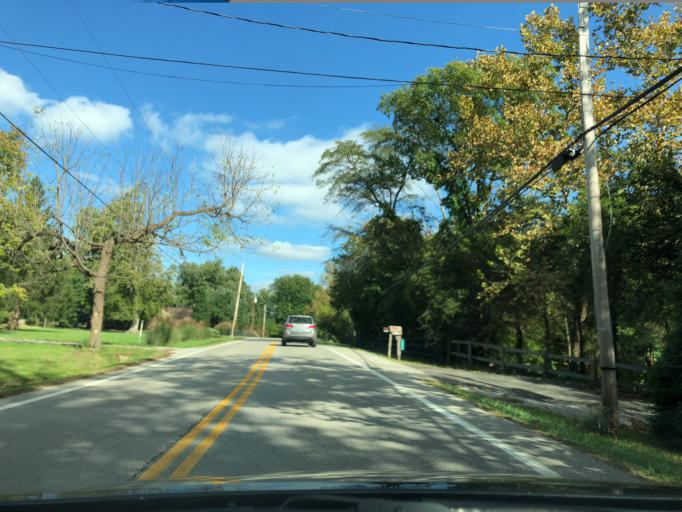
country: US
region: Ohio
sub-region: Hamilton County
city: Loveland
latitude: 39.2796
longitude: -84.2374
